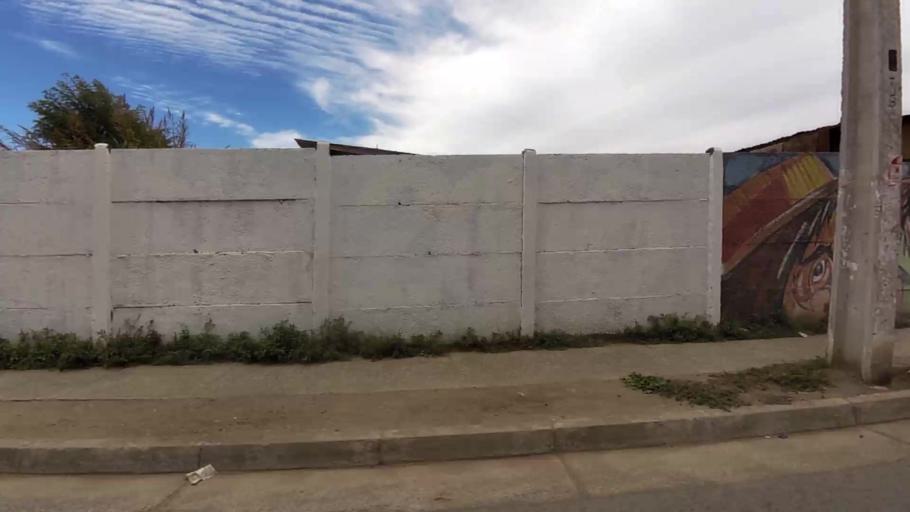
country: CL
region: O'Higgins
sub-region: Provincia de Cachapoal
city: Graneros
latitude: -34.0678
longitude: -70.7350
